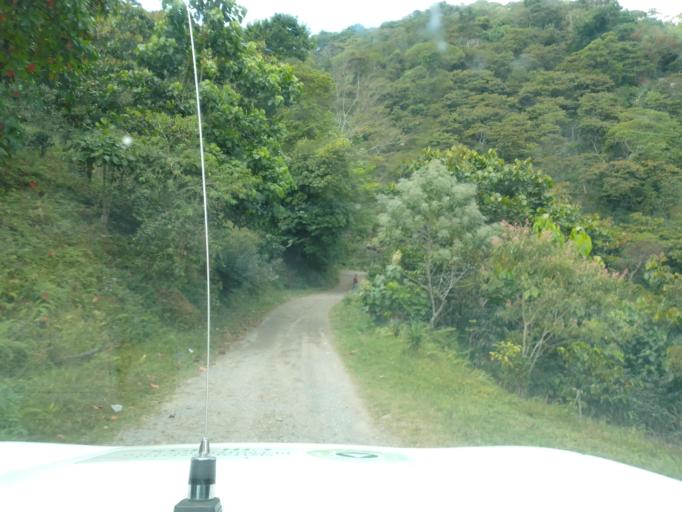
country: MX
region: Chiapas
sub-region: Union Juarez
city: Santo Domingo
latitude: 15.0571
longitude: -92.0975
